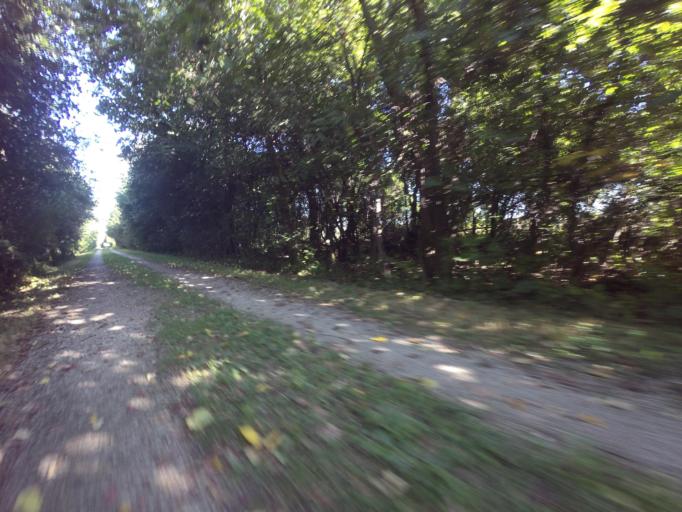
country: CA
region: Ontario
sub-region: Wellington County
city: Guelph
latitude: 43.6569
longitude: -80.4244
